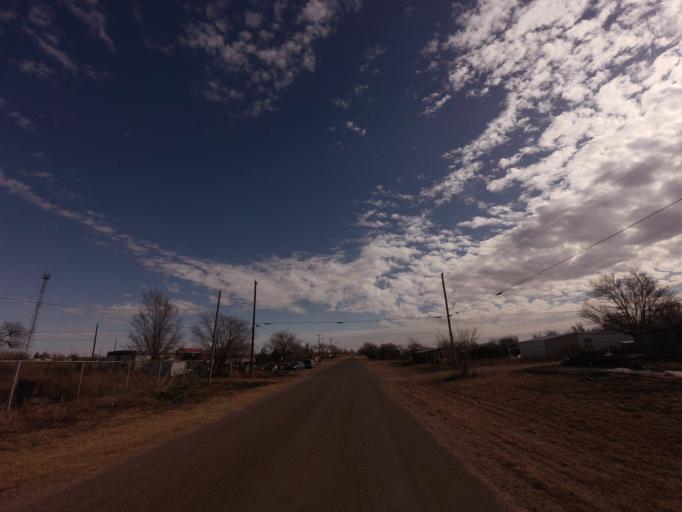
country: US
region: New Mexico
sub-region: Curry County
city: Clovis
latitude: 34.3976
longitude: -103.2314
